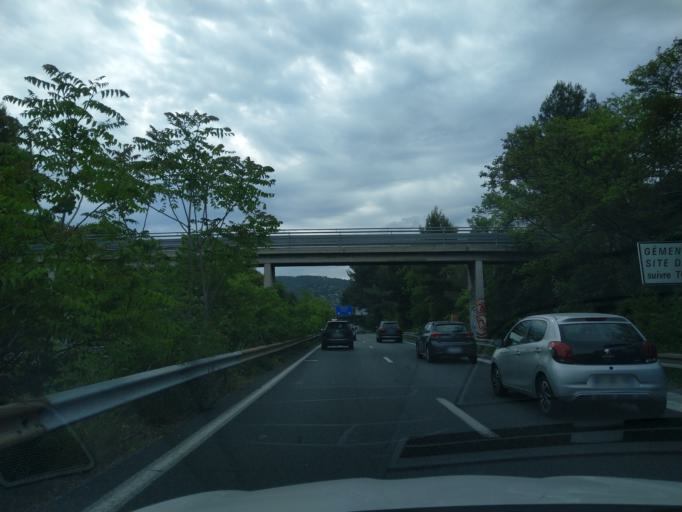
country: FR
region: Provence-Alpes-Cote d'Azur
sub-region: Departement des Bouches-du-Rhone
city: Aubagne
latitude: 43.2852
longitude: 5.5706
